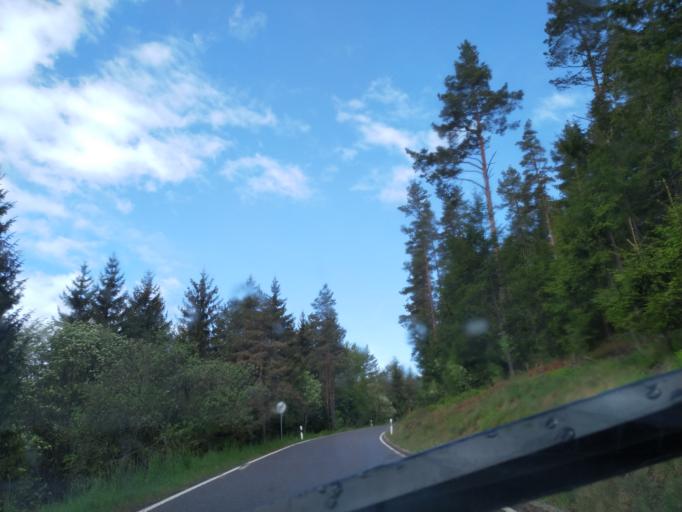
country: DE
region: Baden-Wuerttemberg
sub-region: Freiburg Region
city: Friedenweiler
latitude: 47.9345
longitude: 8.2533
